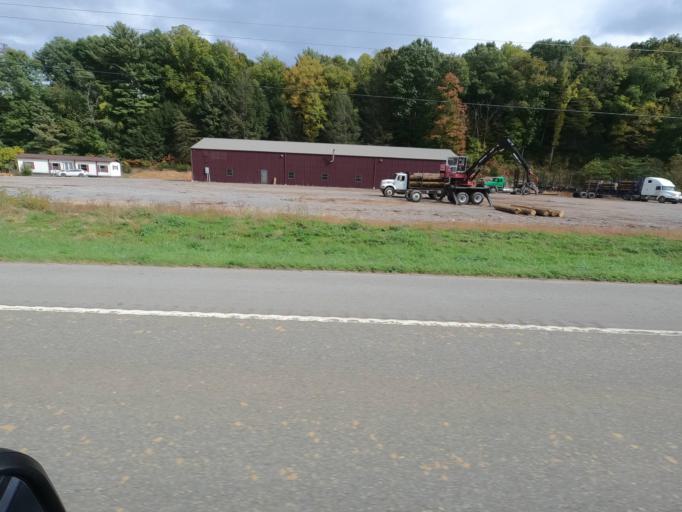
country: US
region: Tennessee
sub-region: Carter County
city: Elizabethton
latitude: 36.2692
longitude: -82.1800
